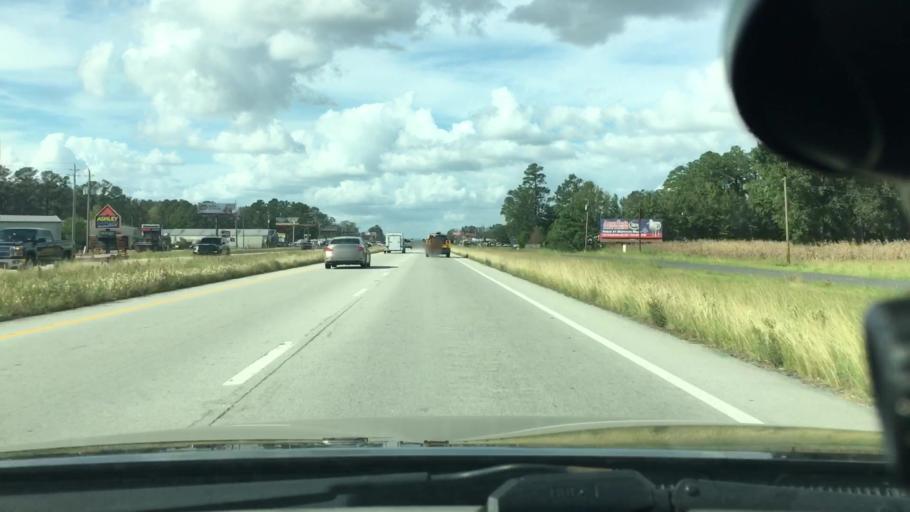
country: US
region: North Carolina
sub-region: Craven County
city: James City
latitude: 35.0580
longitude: -77.0185
